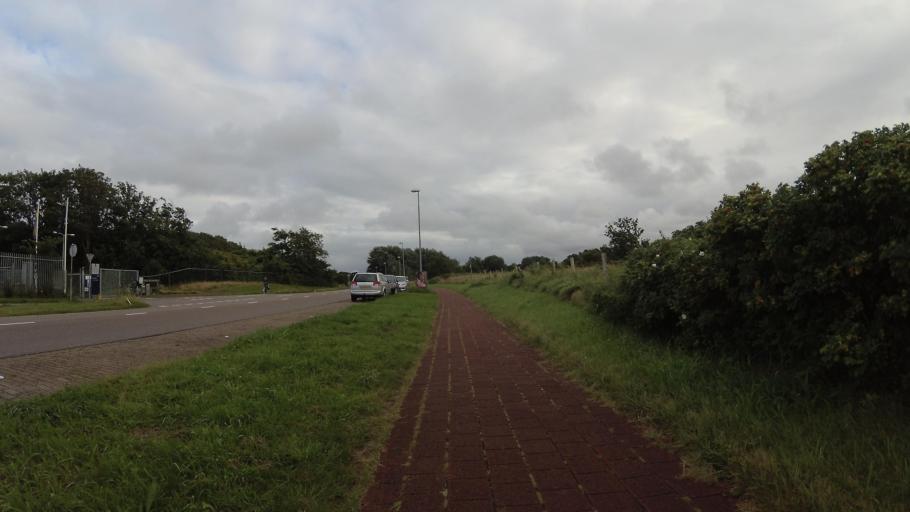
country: NL
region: North Holland
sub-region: Gemeente Den Helder
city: Den Helder
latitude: 52.9445
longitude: 4.7564
